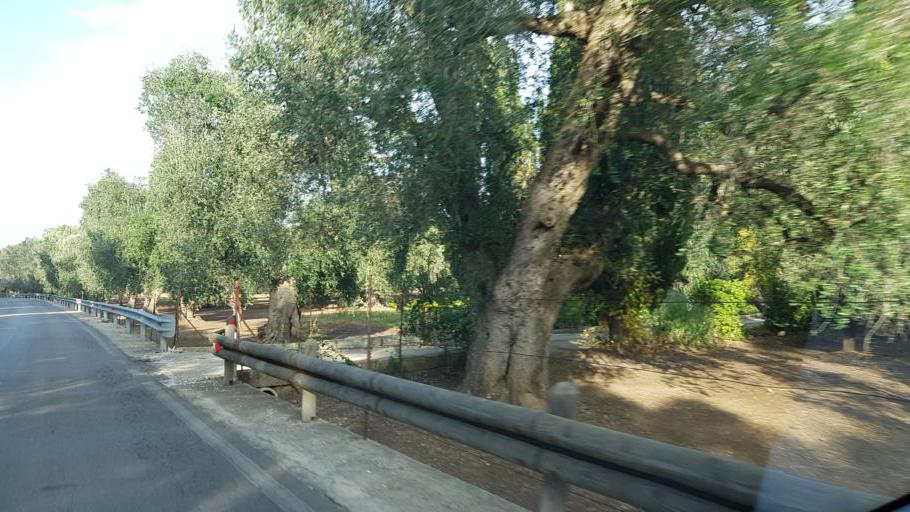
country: IT
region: Apulia
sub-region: Provincia di Brindisi
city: Oria
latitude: 40.5187
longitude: 17.6518
